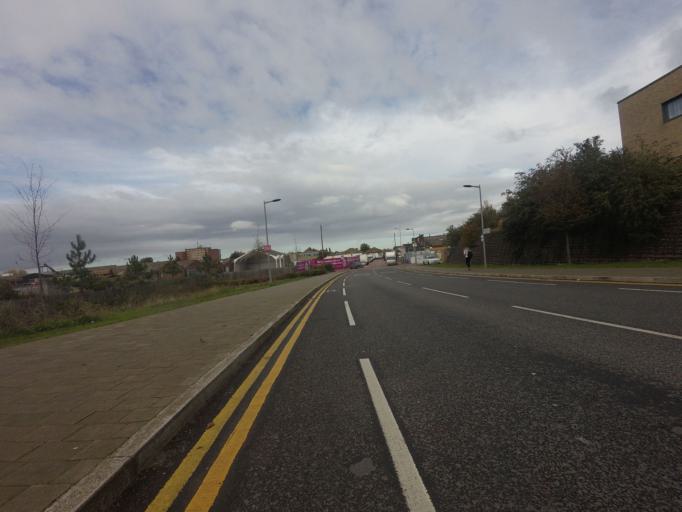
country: GB
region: England
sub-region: Greater London
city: Barking
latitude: 51.5239
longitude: 0.1017
